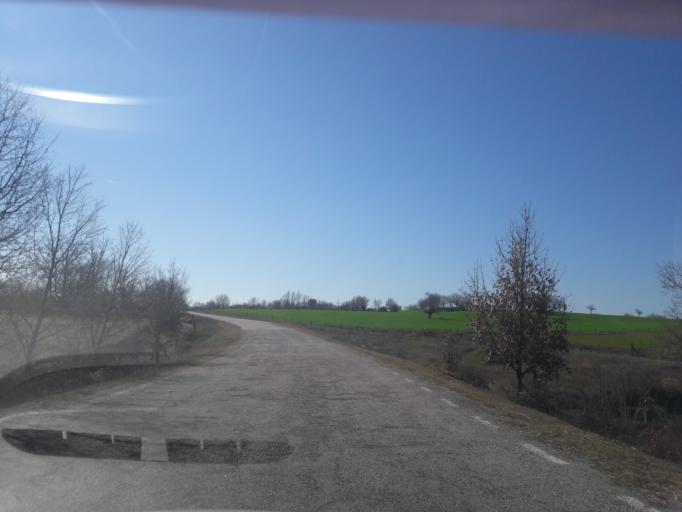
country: ES
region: Castille and Leon
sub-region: Provincia de Salamanca
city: Valsalabroso
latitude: 41.1610
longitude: -6.4959
